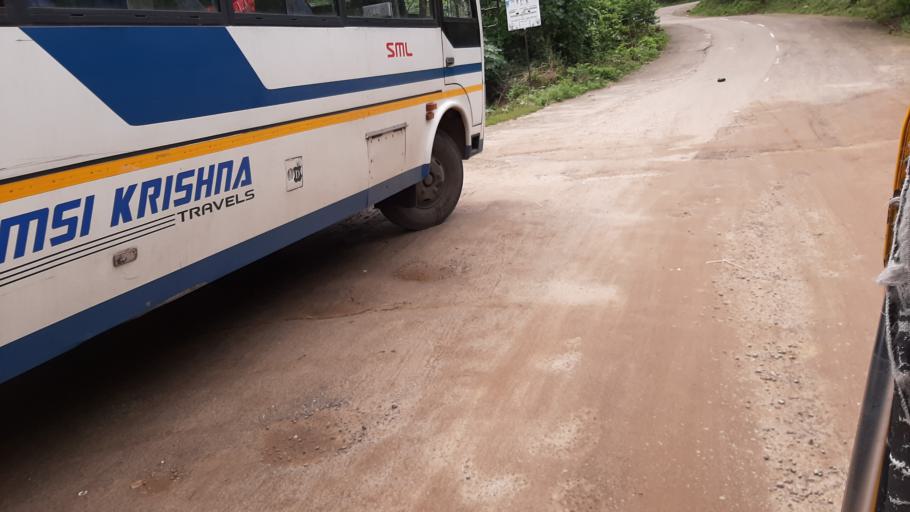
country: IN
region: Andhra Pradesh
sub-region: Vizianagaram District
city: Salur
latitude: 18.2761
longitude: 83.0378
